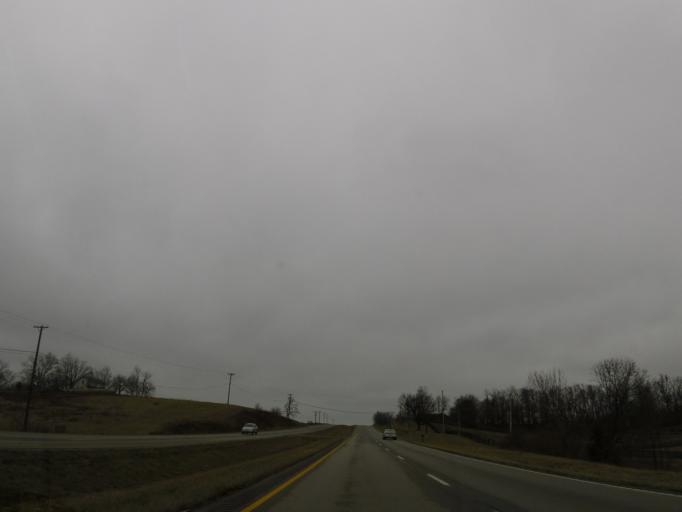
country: US
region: Kentucky
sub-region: Mercer County
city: Jackson
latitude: 37.8098
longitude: -84.8485
